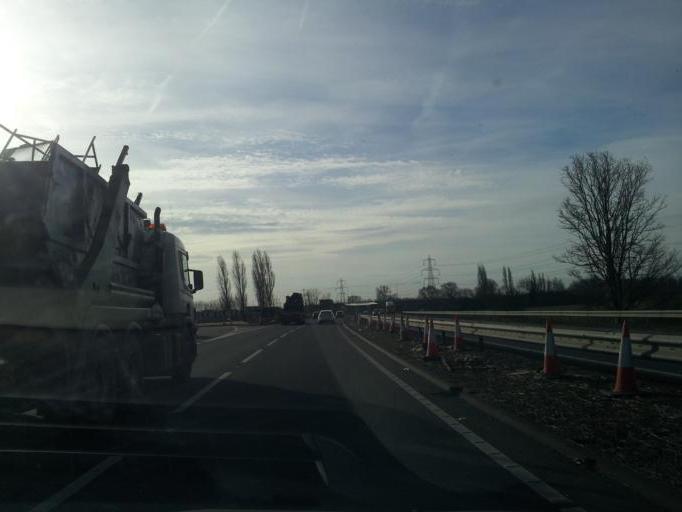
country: GB
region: England
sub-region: Cambridgeshire
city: Eaton Socon
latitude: 52.2090
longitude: -0.2953
